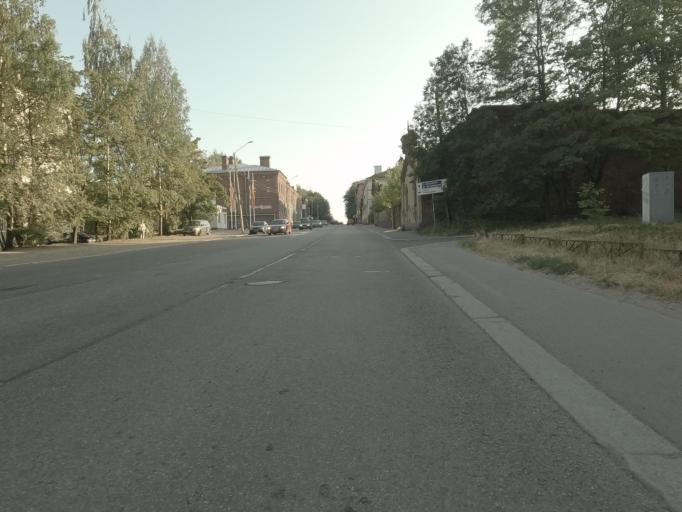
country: RU
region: Leningrad
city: Vyborg
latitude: 60.7192
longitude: 28.7627
